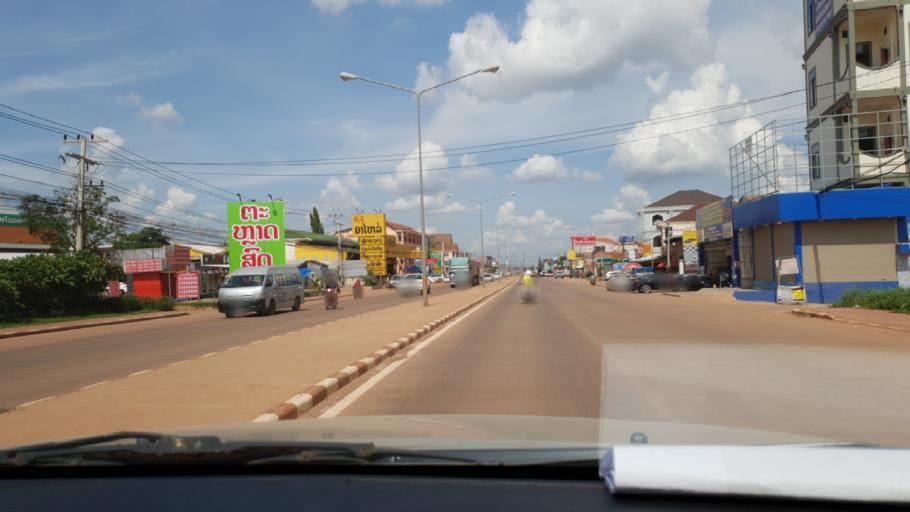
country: LA
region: Vientiane
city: Vientiane
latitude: 18.0325
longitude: 102.6424
